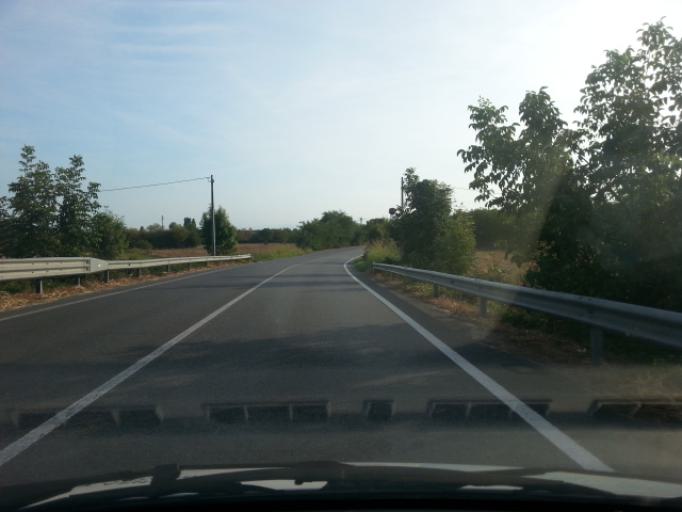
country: IT
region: Piedmont
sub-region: Provincia di Torino
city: Rivalta di Torino
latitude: 45.0235
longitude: 7.5310
